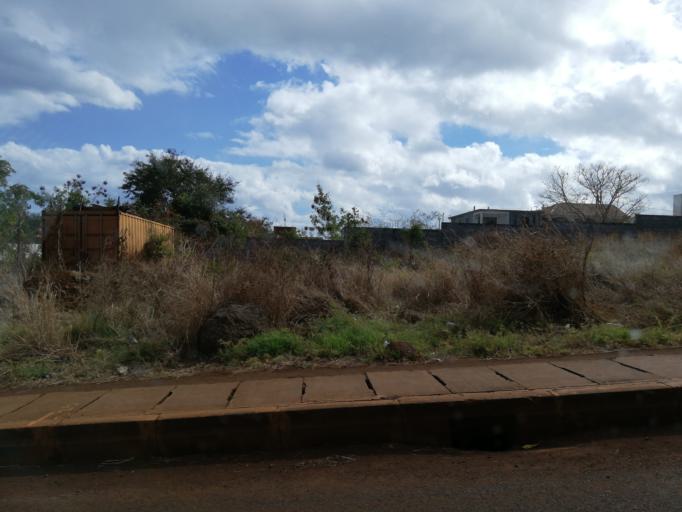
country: MU
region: Black River
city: Petite Riviere
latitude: -20.1925
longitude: 57.4668
